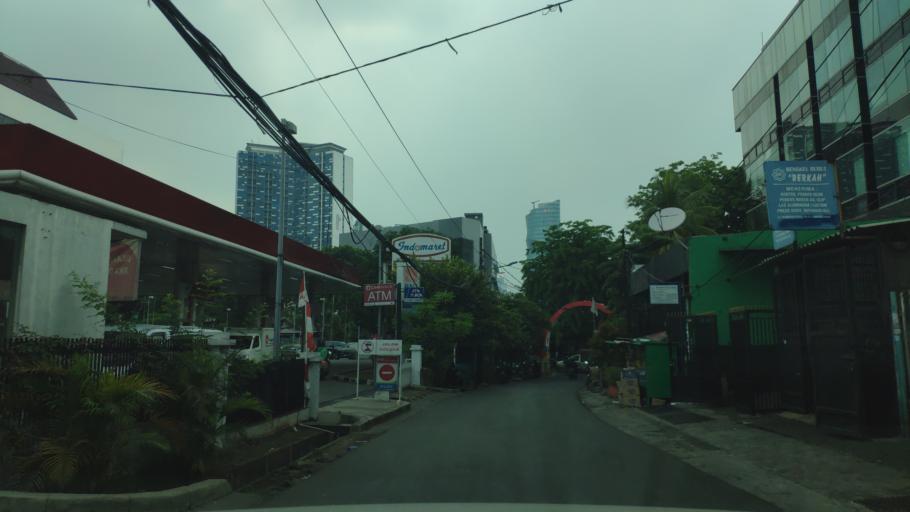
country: ID
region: Jakarta Raya
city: Jakarta
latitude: -6.2039
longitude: 106.7966
